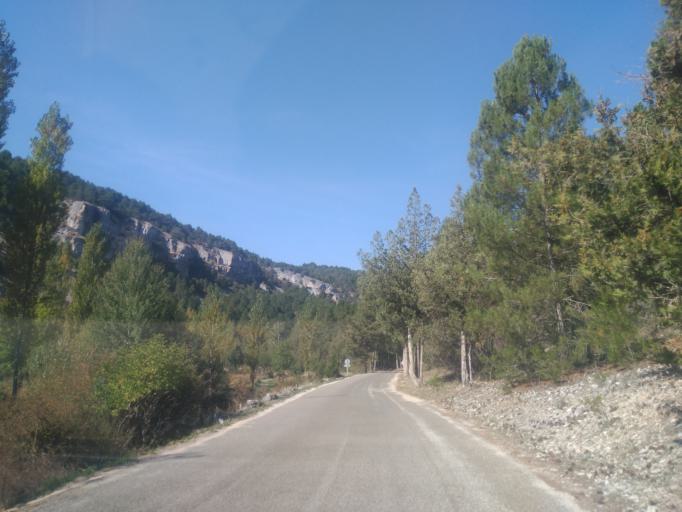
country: ES
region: Castille and Leon
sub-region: Provincia de Soria
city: Ucero
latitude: 41.7389
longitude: -3.0518
